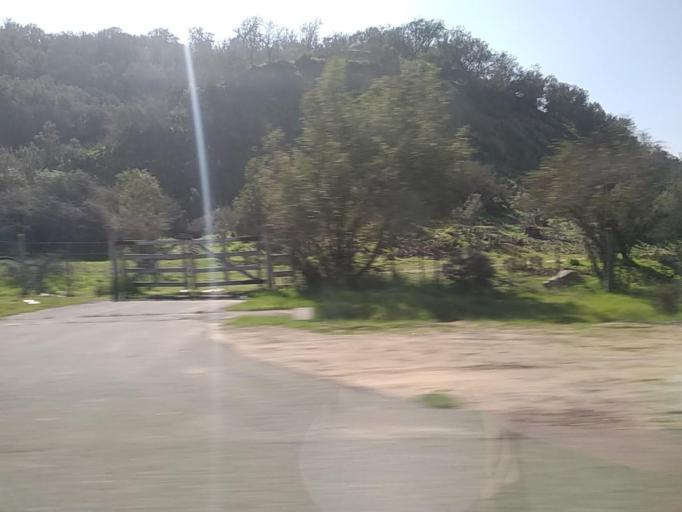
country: CL
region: Valparaiso
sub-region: San Antonio Province
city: El Tabo
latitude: -33.3878
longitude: -71.4582
